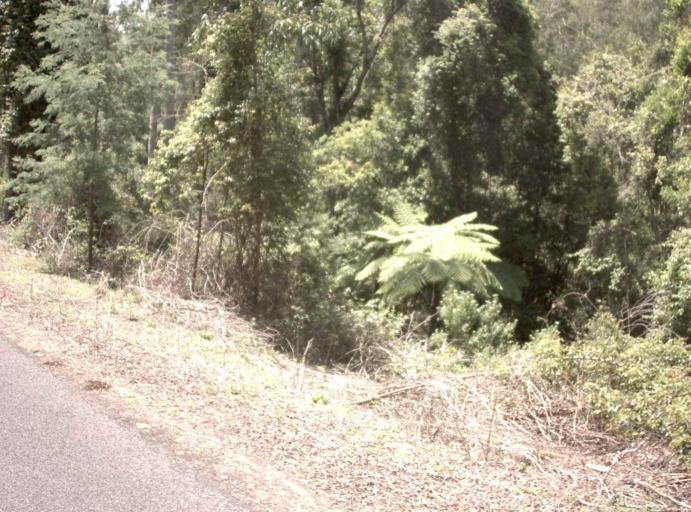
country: AU
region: New South Wales
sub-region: Bombala
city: Bombala
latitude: -37.4559
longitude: 148.9346
